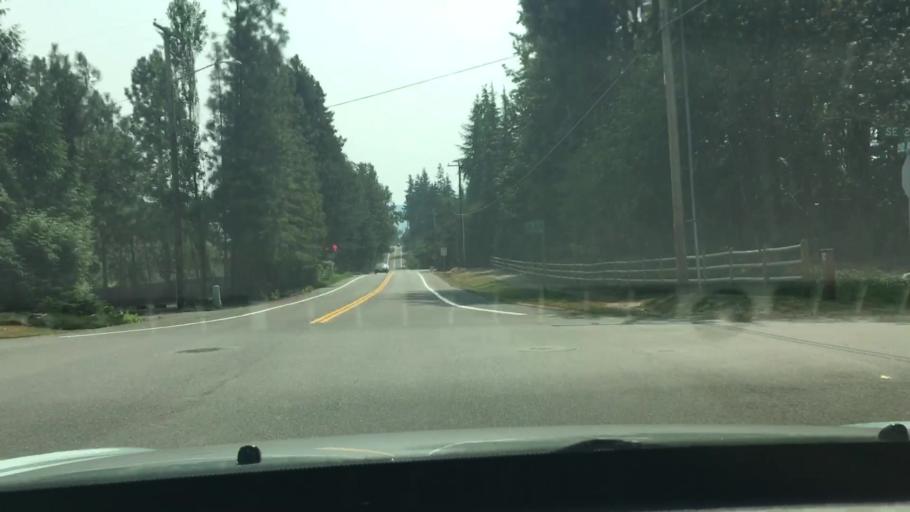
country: US
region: Washington
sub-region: King County
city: City of Sammamish
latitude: 47.5879
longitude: -122.0568
